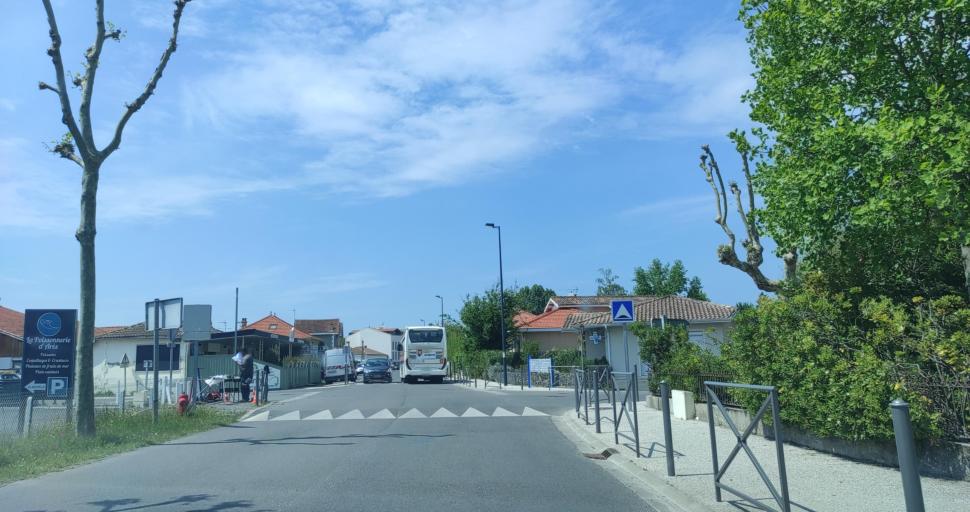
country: FR
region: Aquitaine
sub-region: Departement de la Gironde
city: Ares
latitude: 44.7650
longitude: -1.1360
